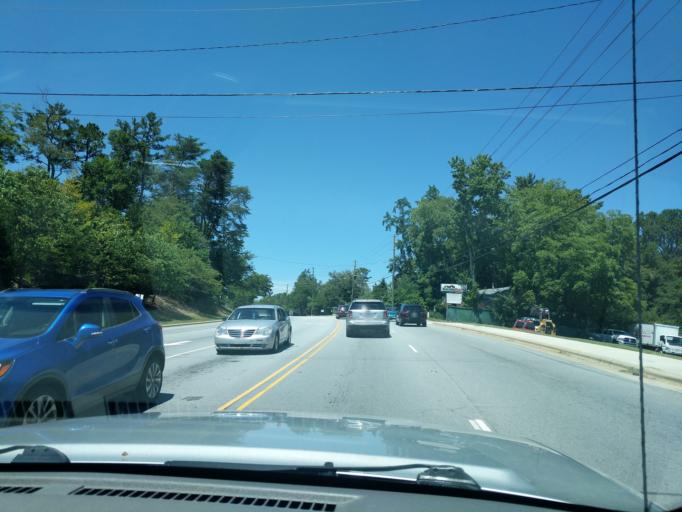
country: US
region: North Carolina
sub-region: Buncombe County
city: Biltmore Forest
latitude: 35.5339
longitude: -82.5278
